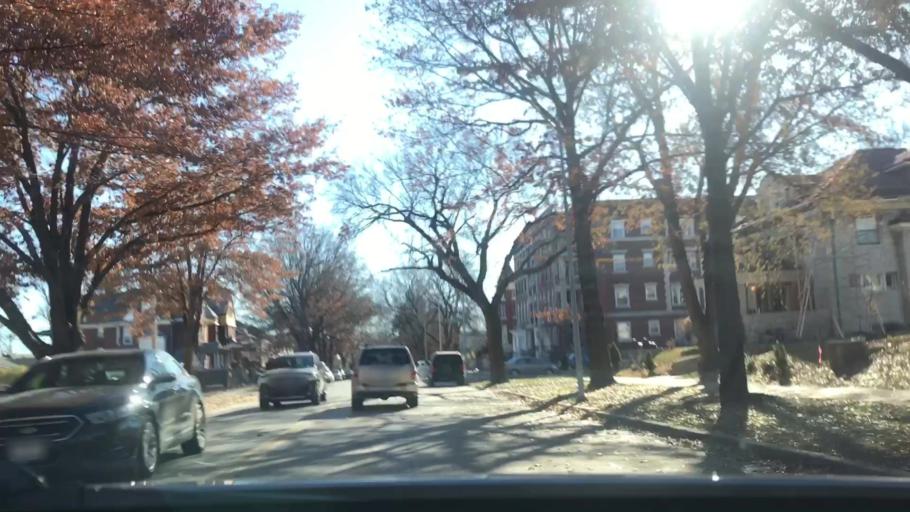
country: US
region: Missouri
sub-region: Clay County
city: North Kansas City
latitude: 39.1086
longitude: -94.5459
